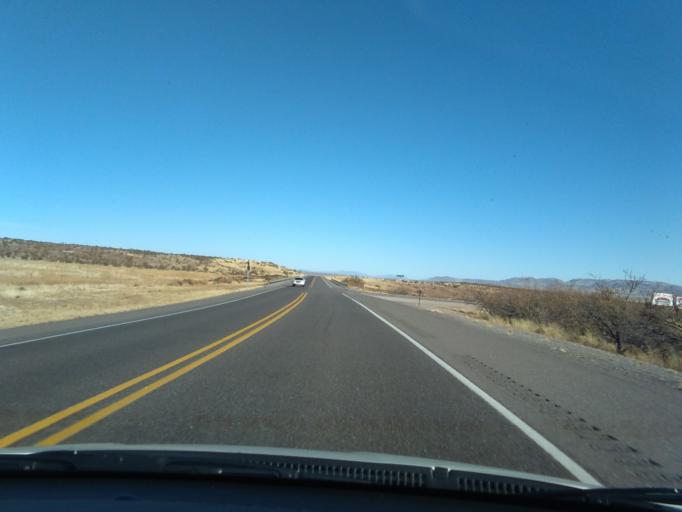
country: US
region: New Mexico
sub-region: Dona Ana County
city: Hatch
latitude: 32.5738
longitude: -107.4031
